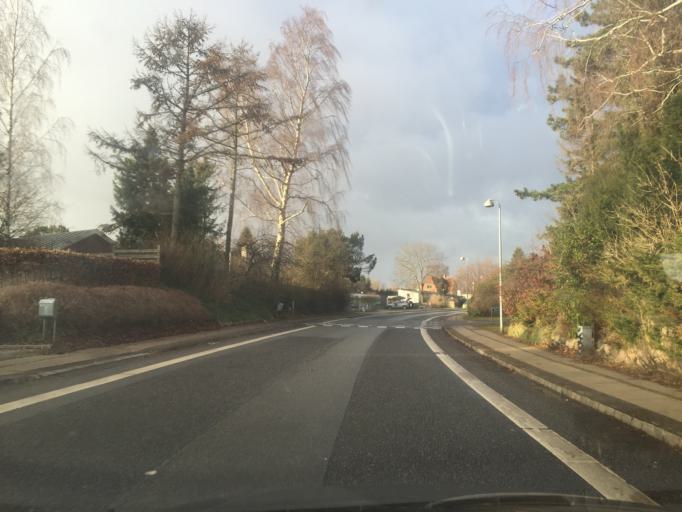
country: DK
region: Capital Region
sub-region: Fureso Kommune
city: Vaerlose
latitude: 55.7558
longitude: 12.4056
